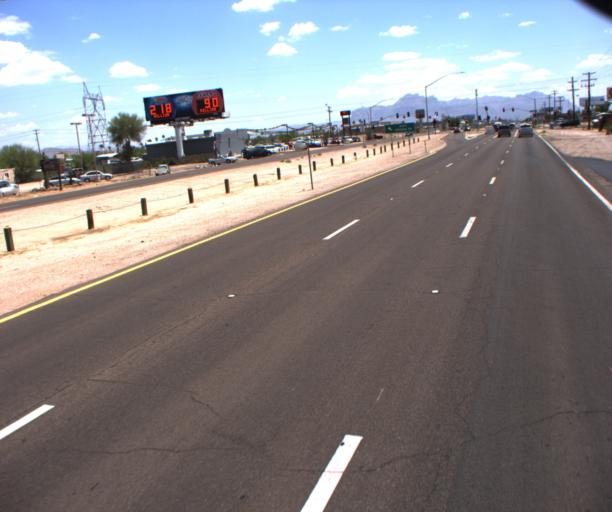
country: US
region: Arizona
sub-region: Pinal County
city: Apache Junction
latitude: 33.4151
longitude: -111.6175
